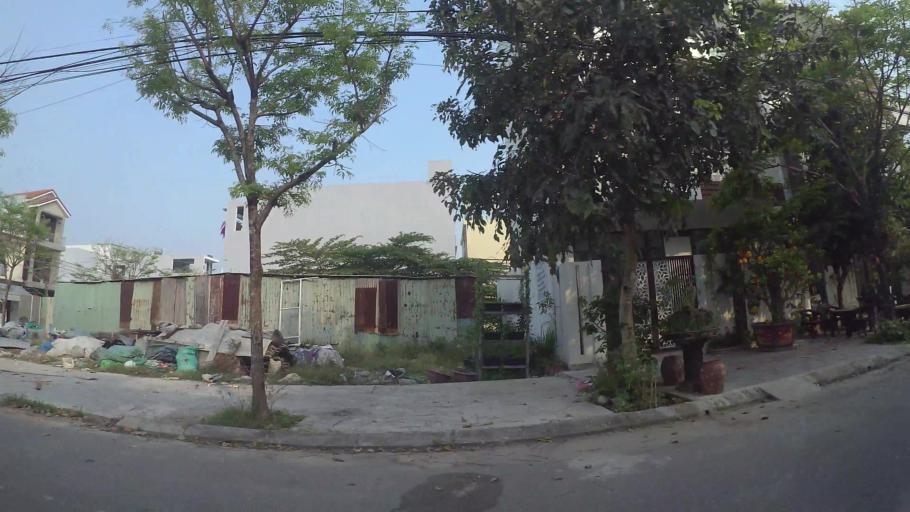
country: VN
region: Da Nang
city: Cam Le
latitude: 16.0100
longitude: 108.2205
